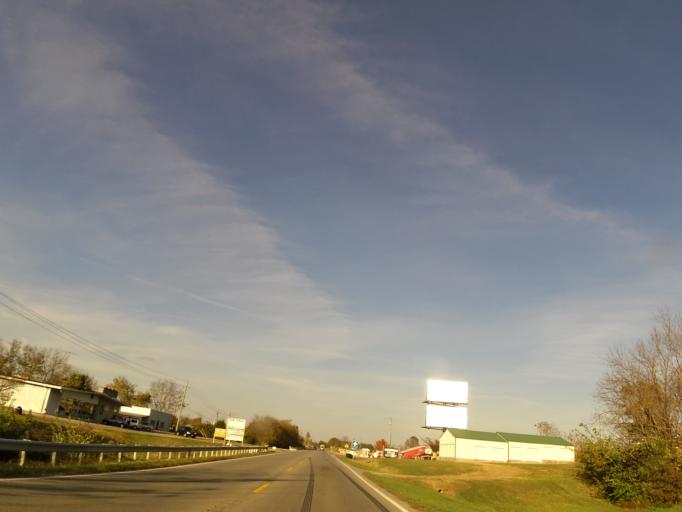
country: US
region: Kentucky
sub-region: Garrard County
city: Lancaster
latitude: 37.5860
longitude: -84.6026
